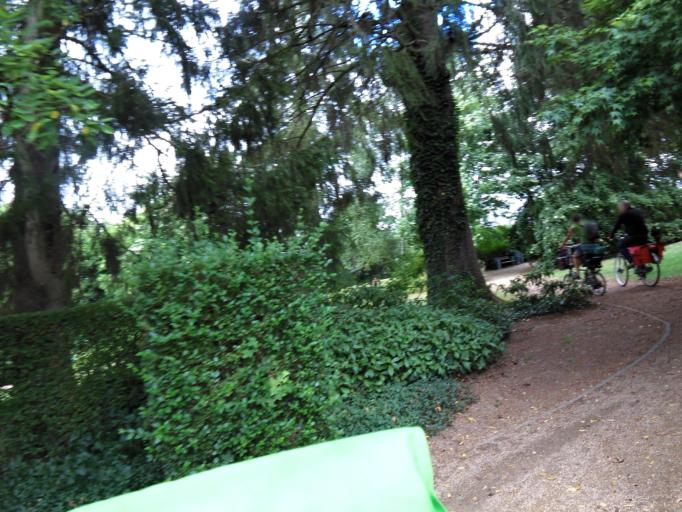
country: BE
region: Wallonia
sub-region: Province de Namur
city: Bievre
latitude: 49.9382
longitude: 5.0211
